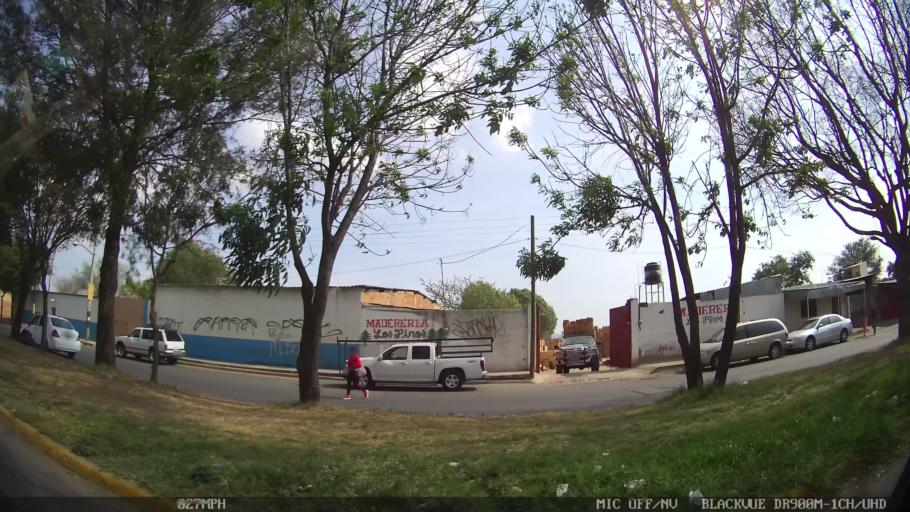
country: MX
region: Jalisco
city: Tonala
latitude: 20.6524
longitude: -103.2247
